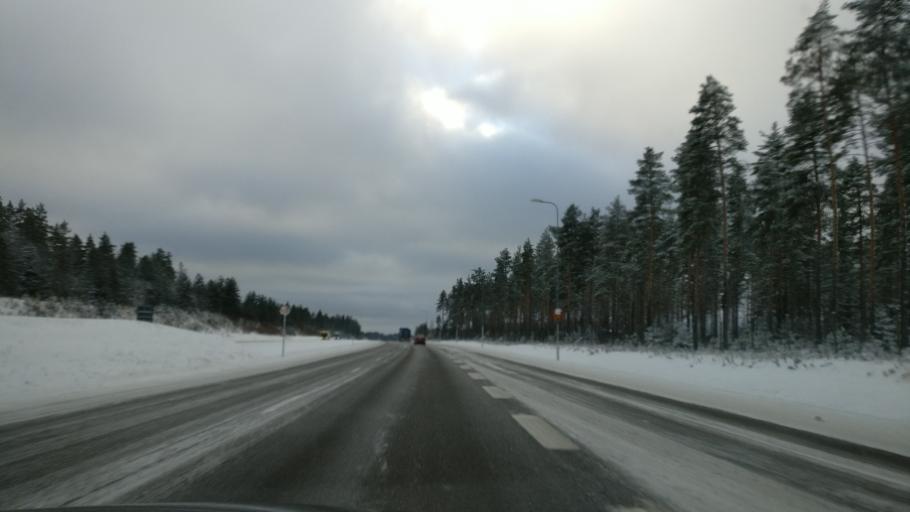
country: FI
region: Paijanne Tavastia
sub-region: Lahti
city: Heinola
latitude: 61.1106
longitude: 25.9196
